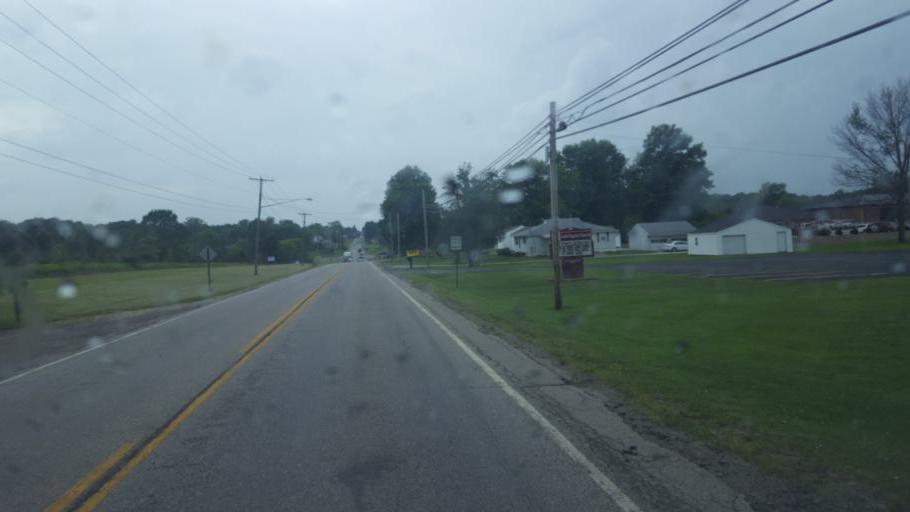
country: US
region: Ohio
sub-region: Richland County
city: Ontario
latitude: 40.7602
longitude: -82.6293
